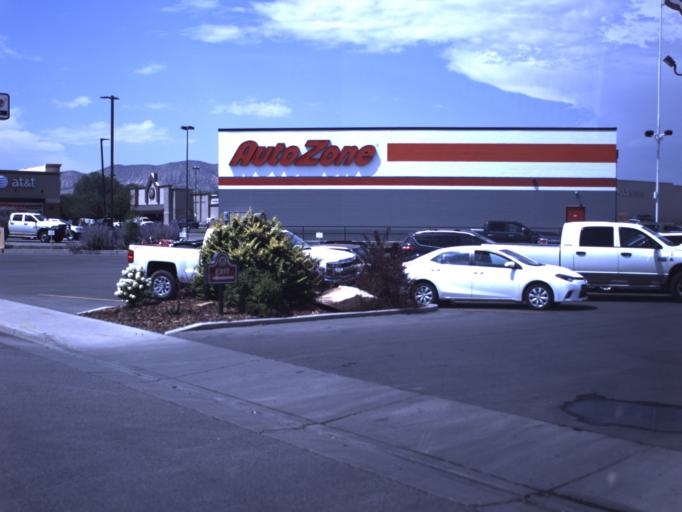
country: US
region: Utah
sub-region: Uintah County
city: Vernal
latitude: 40.4510
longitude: -109.5496
